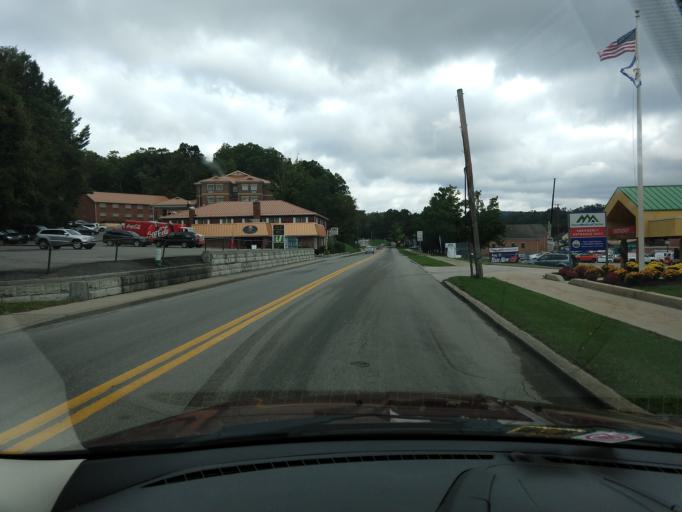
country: US
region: West Virginia
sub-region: Randolph County
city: Elkins
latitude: 38.9286
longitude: -79.8555
